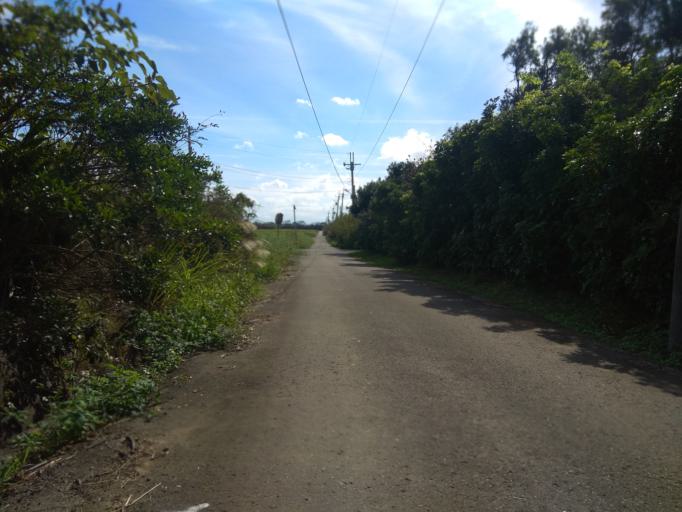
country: TW
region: Taiwan
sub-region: Hsinchu
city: Zhubei
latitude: 25.0196
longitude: 121.0629
